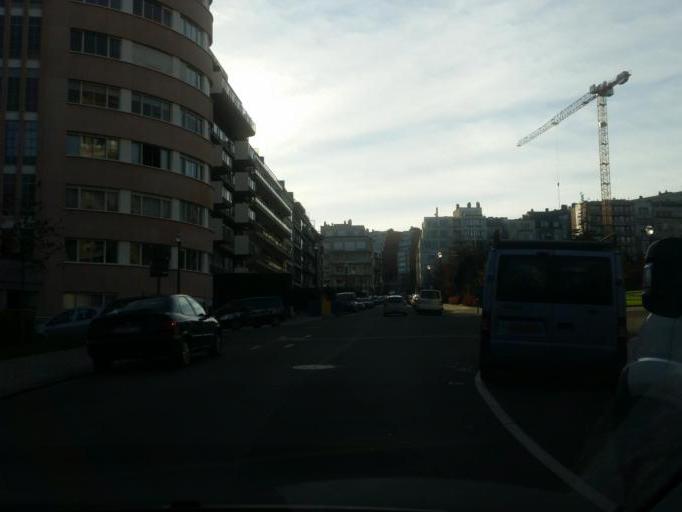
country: BE
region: Brussels Capital
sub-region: Bruxelles-Capitale
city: Brussels
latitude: 50.8223
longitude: 4.3733
